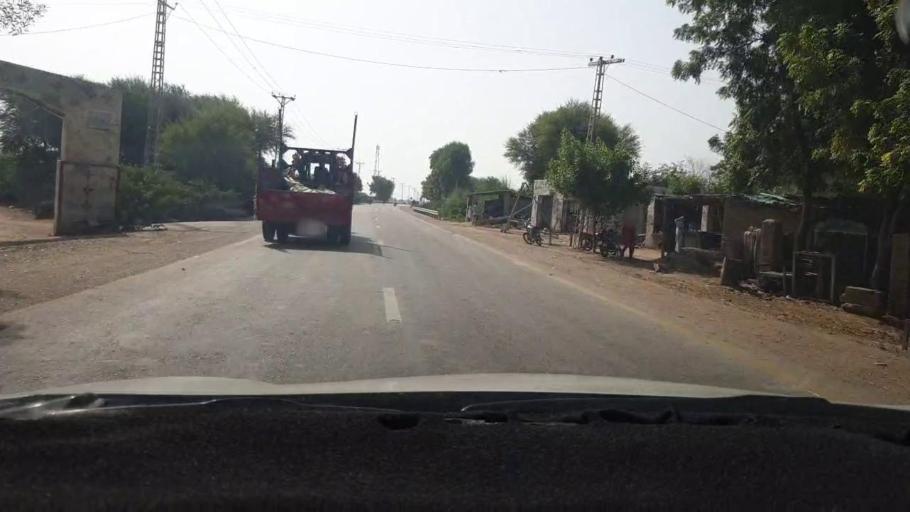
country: PK
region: Sindh
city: Jhol
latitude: 25.9426
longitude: 68.9860
